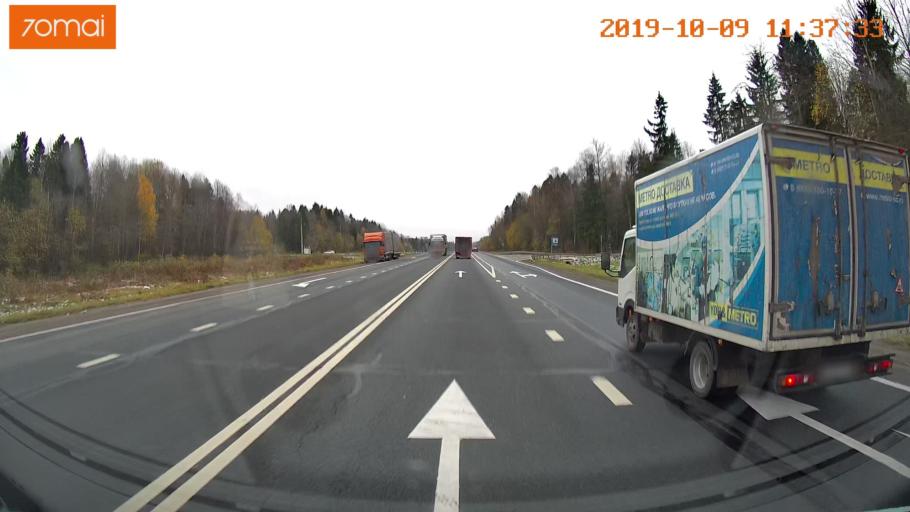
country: RU
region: Vologda
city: Gryazovets
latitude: 58.9781
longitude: 40.1474
